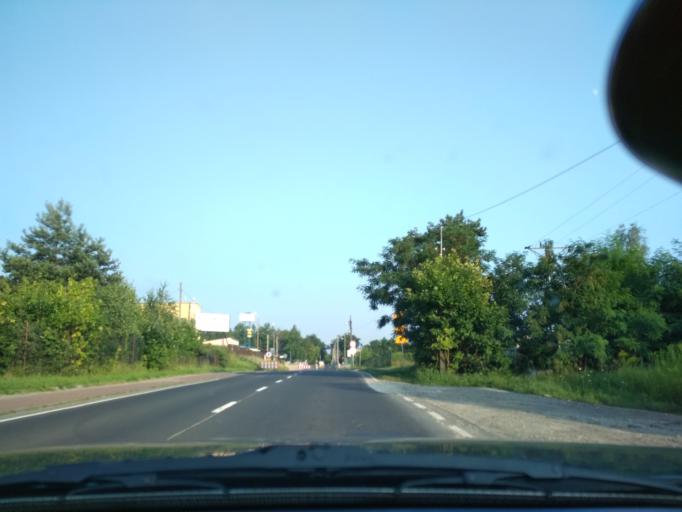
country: PL
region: Silesian Voivodeship
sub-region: Powiat zawiercianski
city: Ogrodzieniec
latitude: 50.4654
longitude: 19.4903
